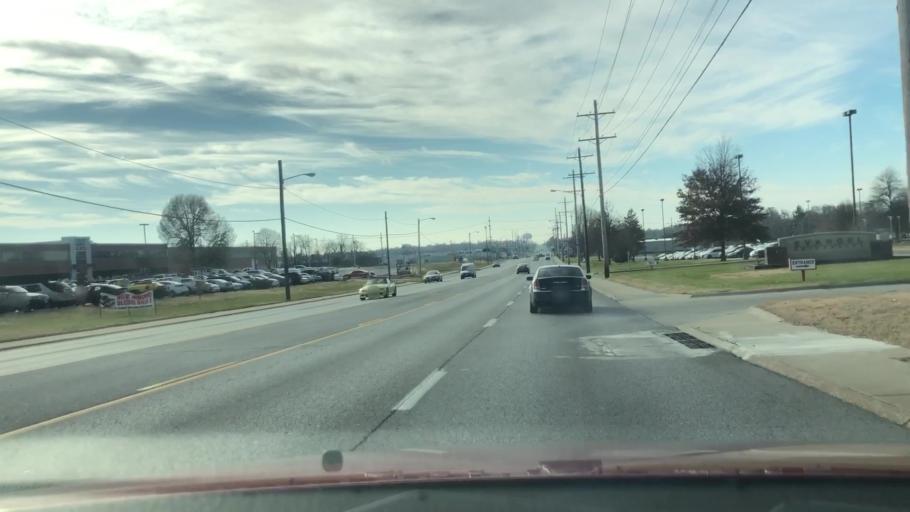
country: US
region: Missouri
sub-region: Greene County
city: Springfield
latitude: 37.2214
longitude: -93.2616
